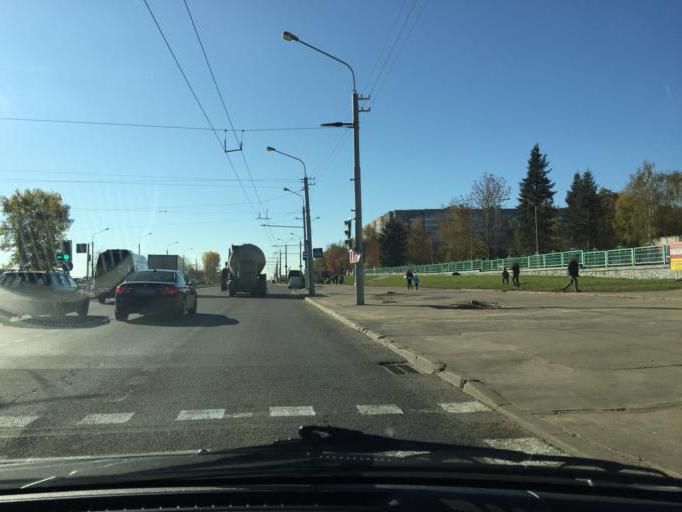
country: BY
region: Minsk
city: Syenitsa
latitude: 53.8505
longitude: 27.5367
